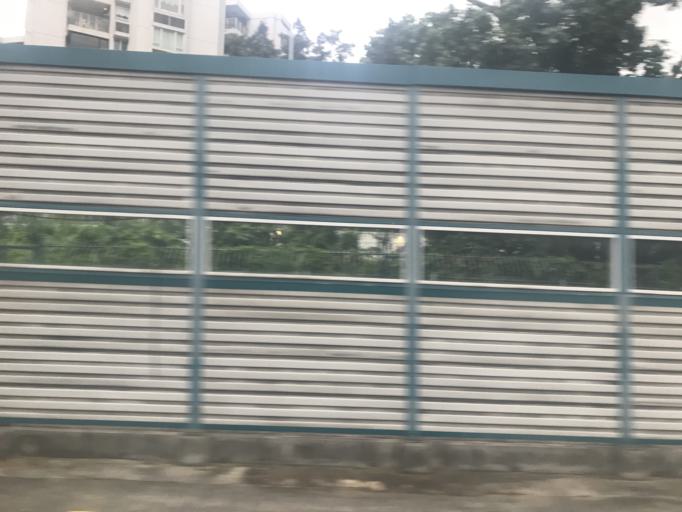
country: HK
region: Wong Tai Sin
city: Wong Tai Sin
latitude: 22.3347
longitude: 114.1766
